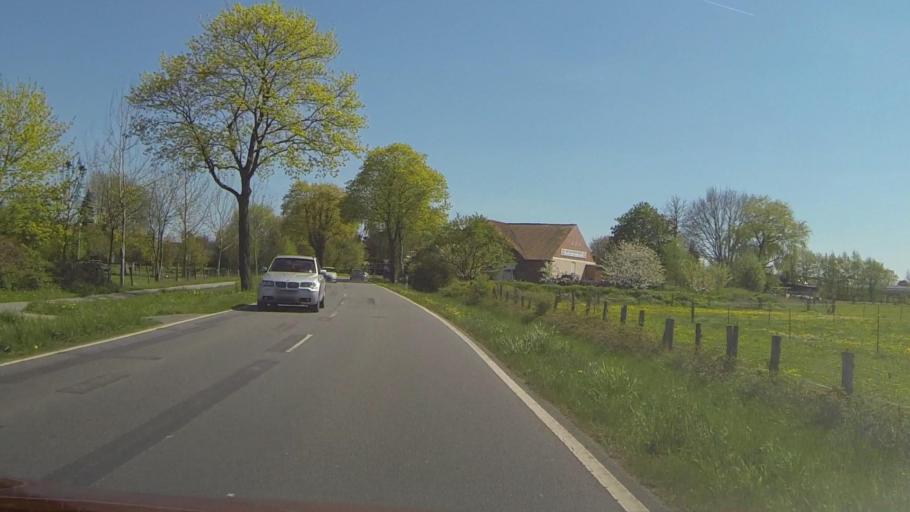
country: DE
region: Schleswig-Holstein
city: Ellerbek
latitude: 53.6497
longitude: 9.8713
